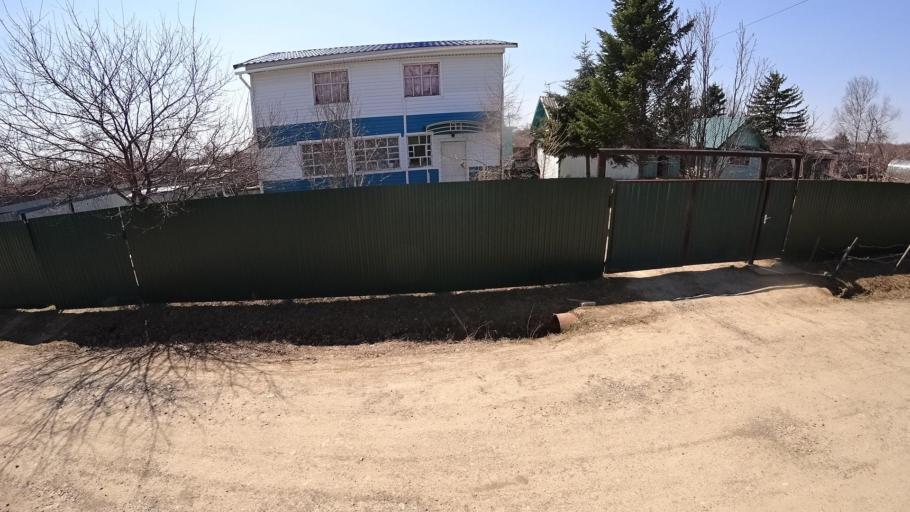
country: RU
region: Khabarovsk Krai
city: Khurba
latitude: 50.4121
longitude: 136.8673
